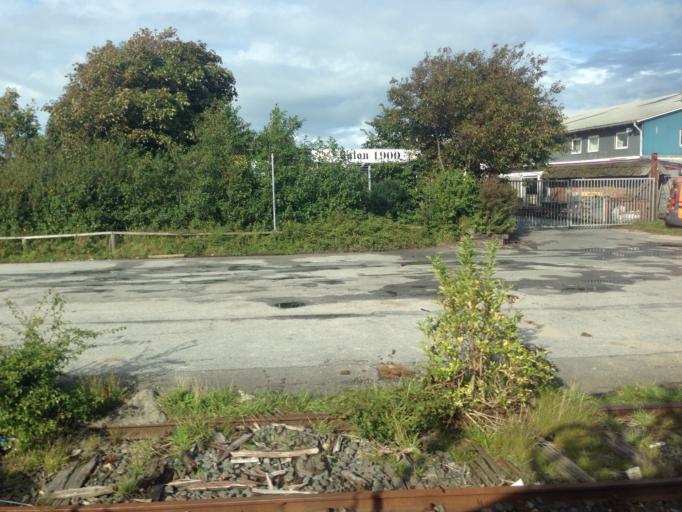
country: DE
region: Schleswig-Holstein
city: Keitum
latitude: 54.8895
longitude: 8.3674
